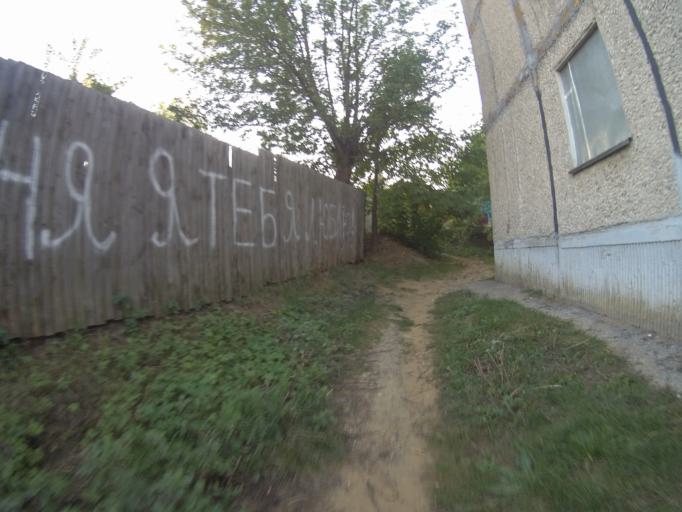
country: RU
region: Vladimir
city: Vladimir
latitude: 56.1129
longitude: 40.3765
